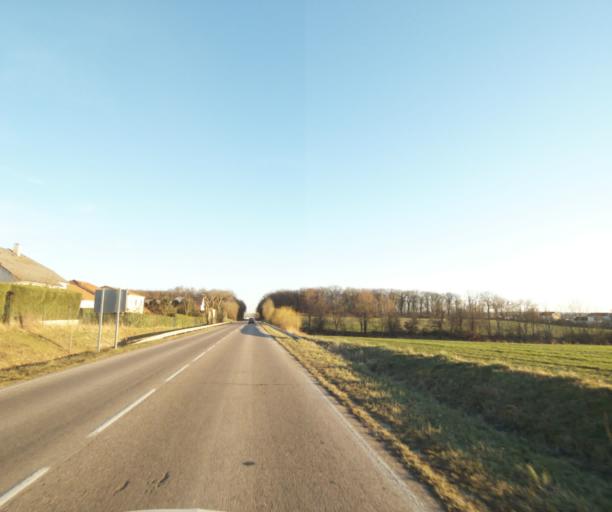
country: FR
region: Lorraine
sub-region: Departement de Meurthe-et-Moselle
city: Laneuveville-devant-Nancy
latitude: 48.6740
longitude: 6.2287
